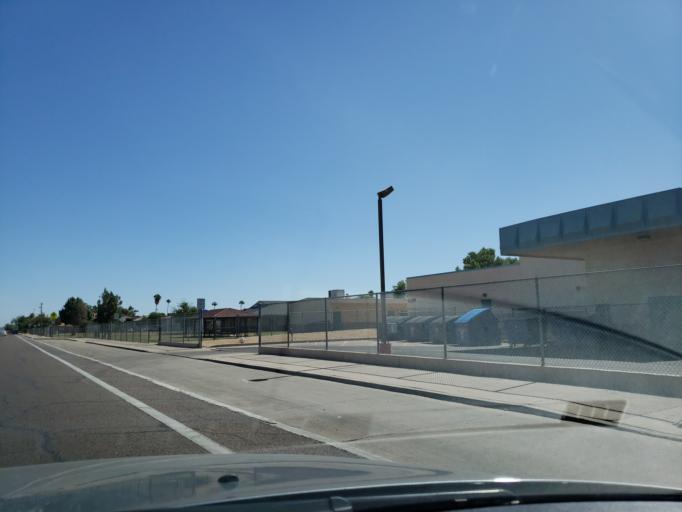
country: US
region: Arizona
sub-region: Maricopa County
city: Glendale
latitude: 33.5022
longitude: -112.1769
